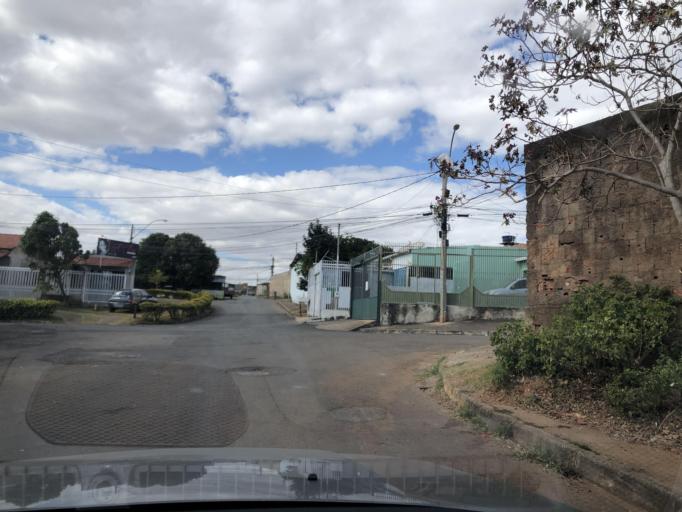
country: BR
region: Federal District
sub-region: Brasilia
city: Brasilia
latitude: -15.8859
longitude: -48.1297
